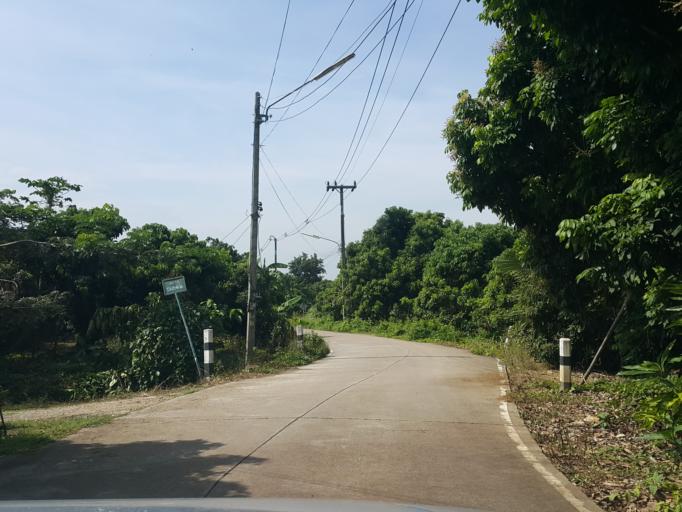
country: TH
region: Chiang Mai
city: Saraphi
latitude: 18.6872
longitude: 99.0691
